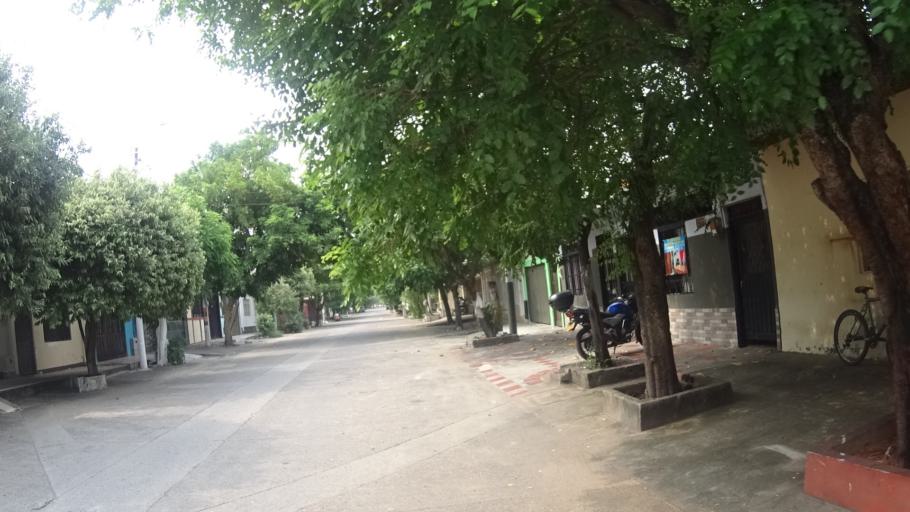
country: CO
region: Caldas
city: La Dorada
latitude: 5.4508
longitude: -74.6670
